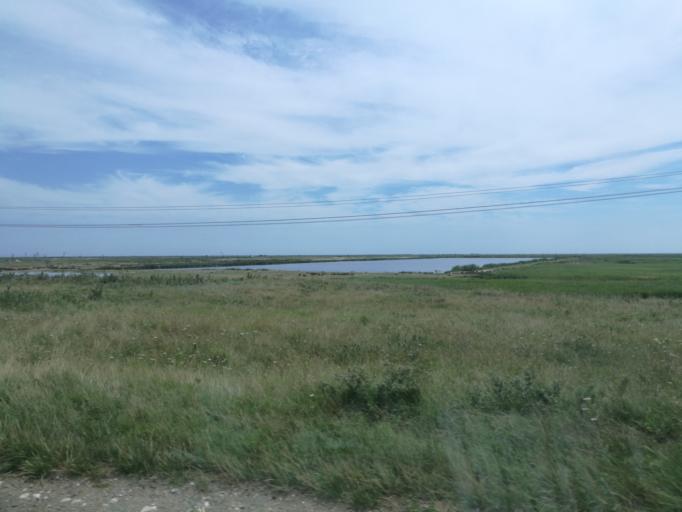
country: RO
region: Constanta
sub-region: Comuna Sacele
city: Sacele
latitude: 44.4448
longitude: 28.7325
